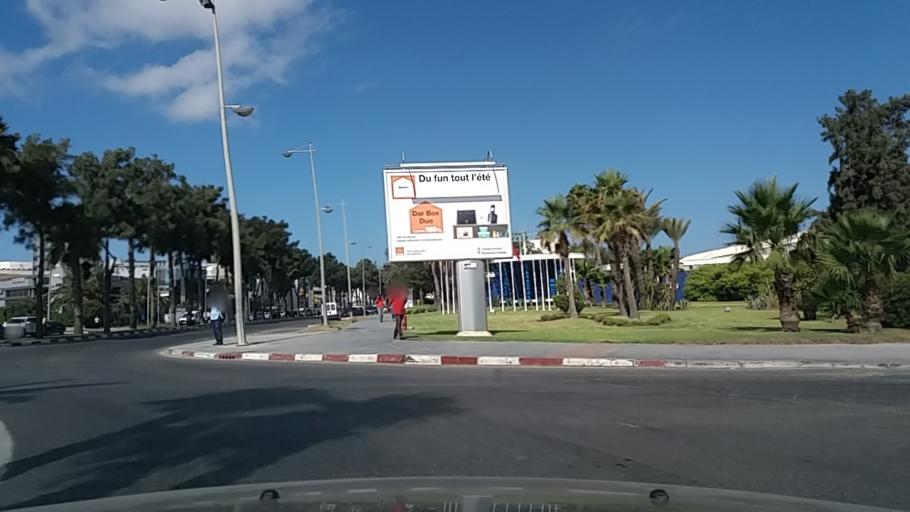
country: MA
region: Tanger-Tetouan
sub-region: Tanger-Assilah
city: Boukhalef
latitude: 35.7156
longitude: -5.9053
